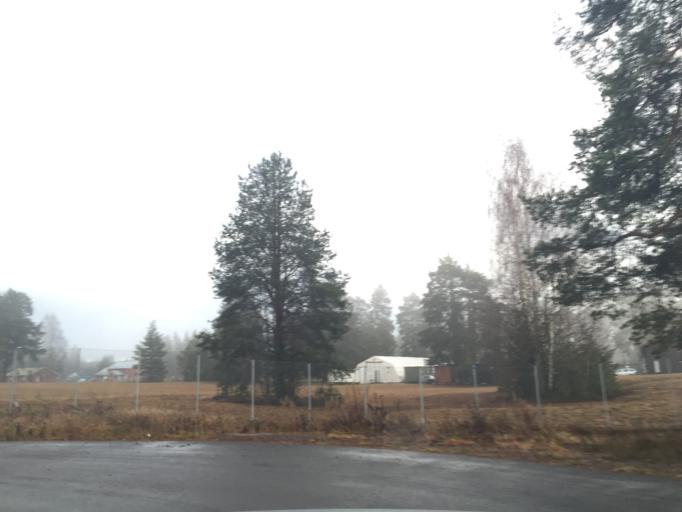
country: NO
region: Hedmark
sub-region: Elverum
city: Elverum
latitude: 60.8796
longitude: 11.5376
